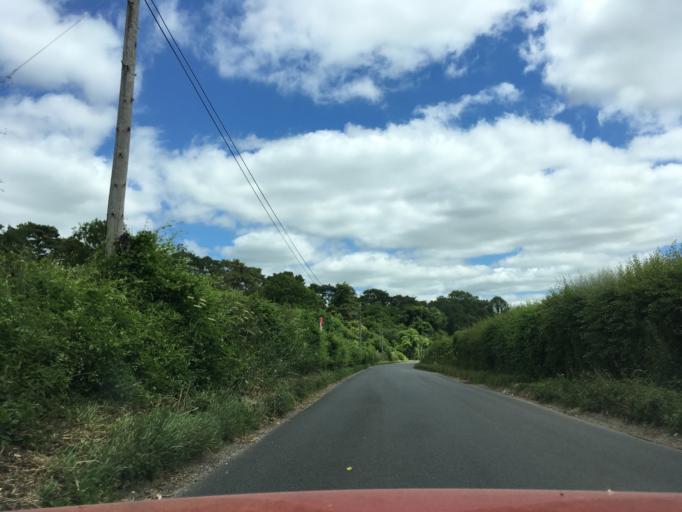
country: GB
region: England
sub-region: Hampshire
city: Highclere
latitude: 51.2391
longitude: -1.3769
